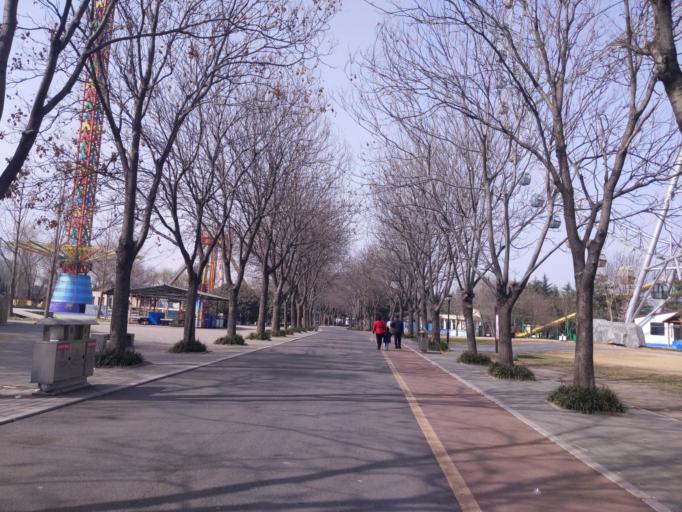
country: CN
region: Henan Sheng
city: Puyang
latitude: 35.7752
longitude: 114.9601
